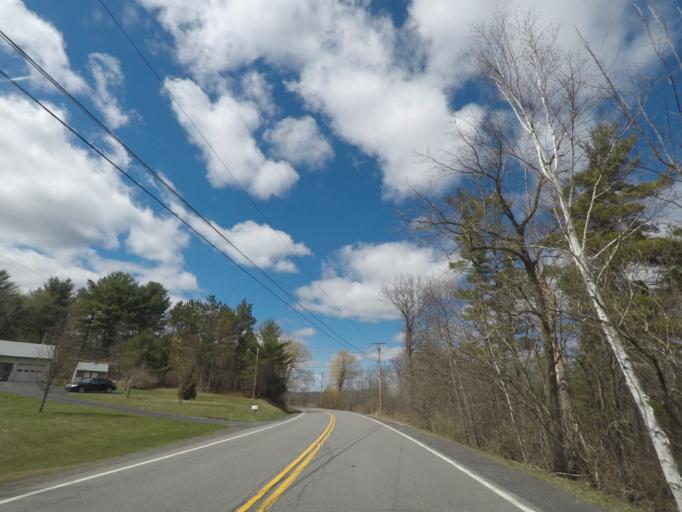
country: US
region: New York
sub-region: Albany County
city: Voorheesville
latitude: 42.6457
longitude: -73.9734
